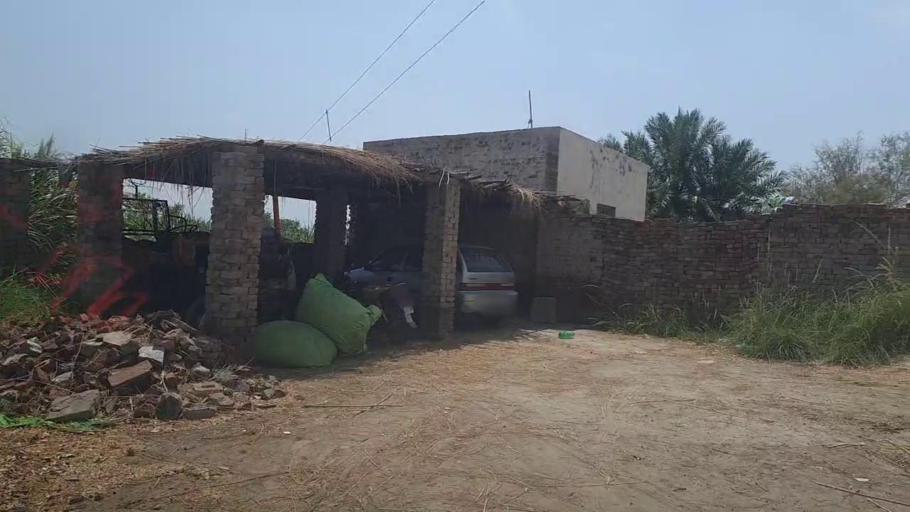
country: PK
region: Sindh
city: Ubauro
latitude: 28.1873
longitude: 69.7710
